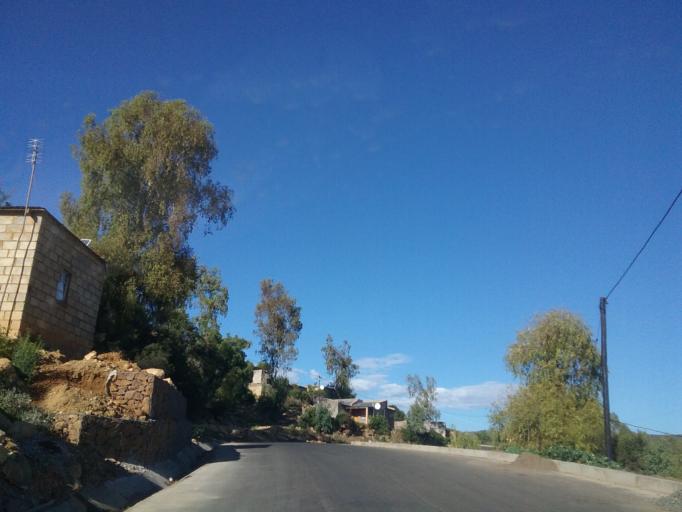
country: LS
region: Quthing
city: Quthing
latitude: -30.4037
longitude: 27.7039
